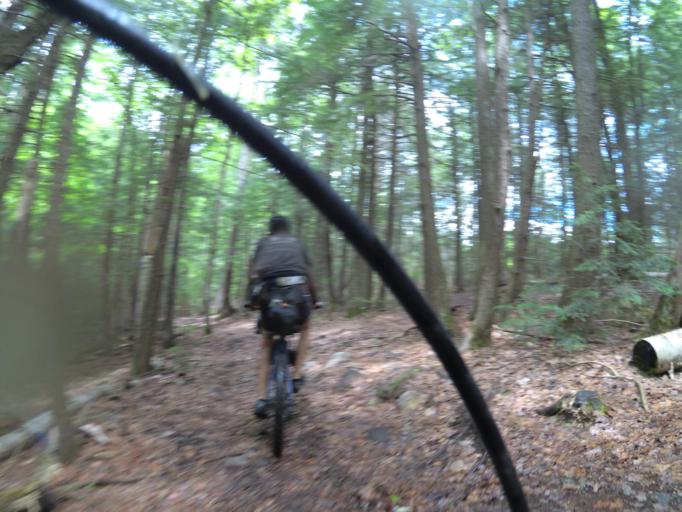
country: CA
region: Ontario
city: Renfrew
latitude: 45.0823
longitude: -76.8932
